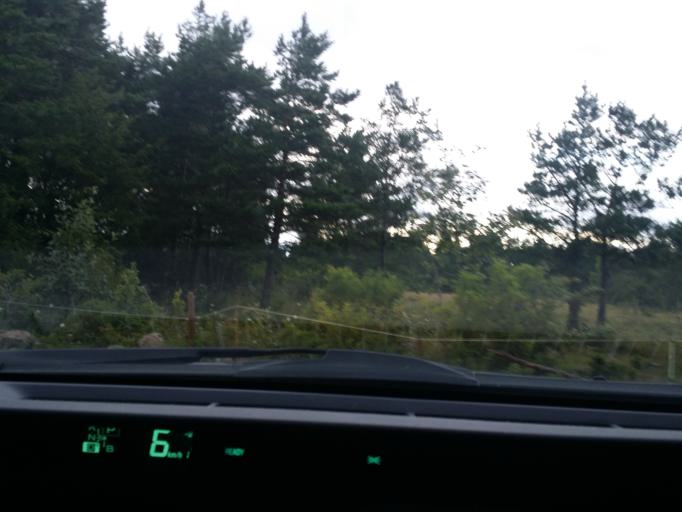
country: SE
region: Kalmar
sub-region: Borgholms Kommun
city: Borgholm
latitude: 57.2045
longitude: 16.9678
